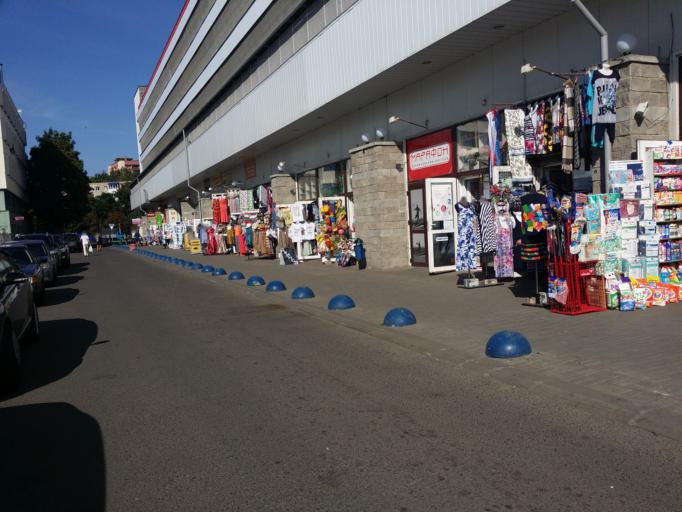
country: BY
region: Minsk
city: Minsk
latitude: 53.9199
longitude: 27.5803
